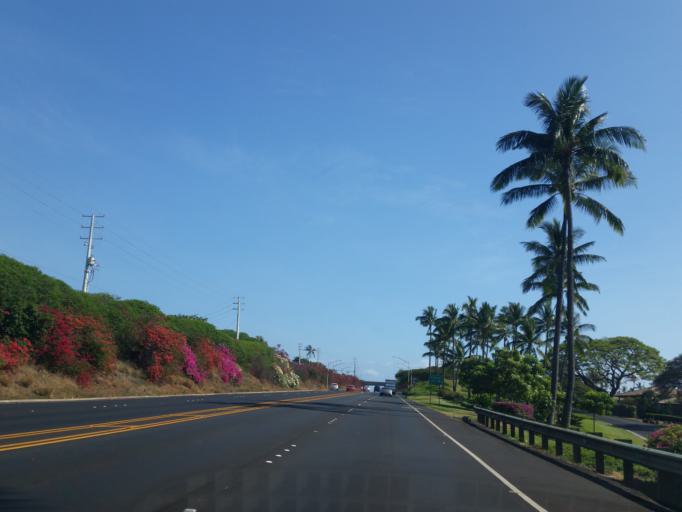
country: US
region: Hawaii
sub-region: Maui County
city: Kaanapali Landing
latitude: 20.9301
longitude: -156.6901
